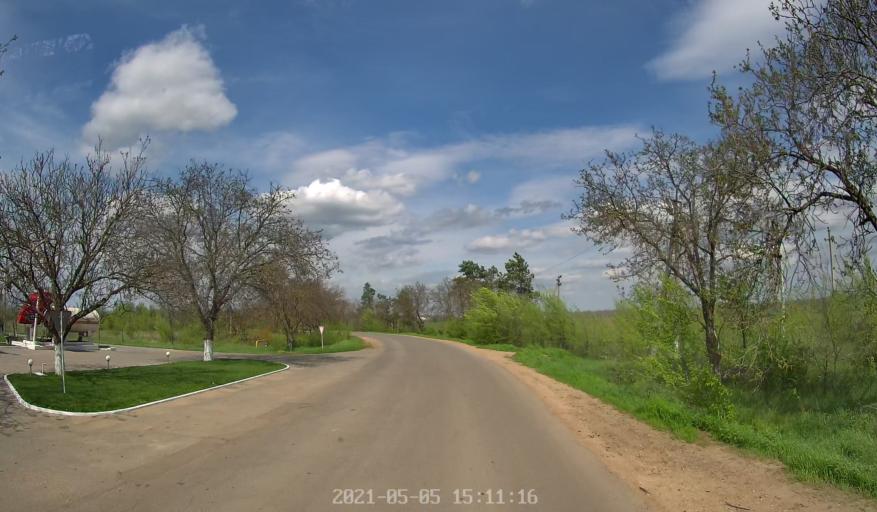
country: MD
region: Chisinau
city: Vadul lui Voda
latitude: 47.1007
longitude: 29.1912
